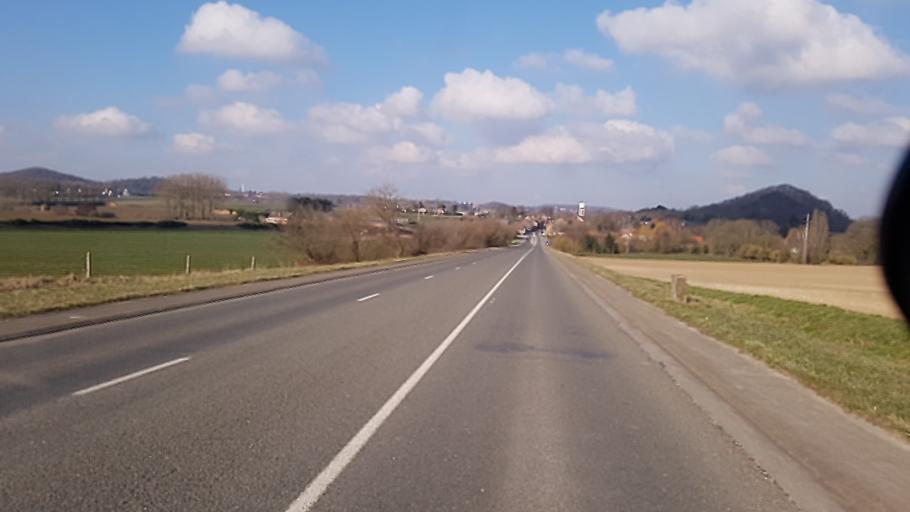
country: BE
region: Wallonia
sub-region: Province du Hainaut
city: Quevy-le-Petit
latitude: 50.3988
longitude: 3.9381
